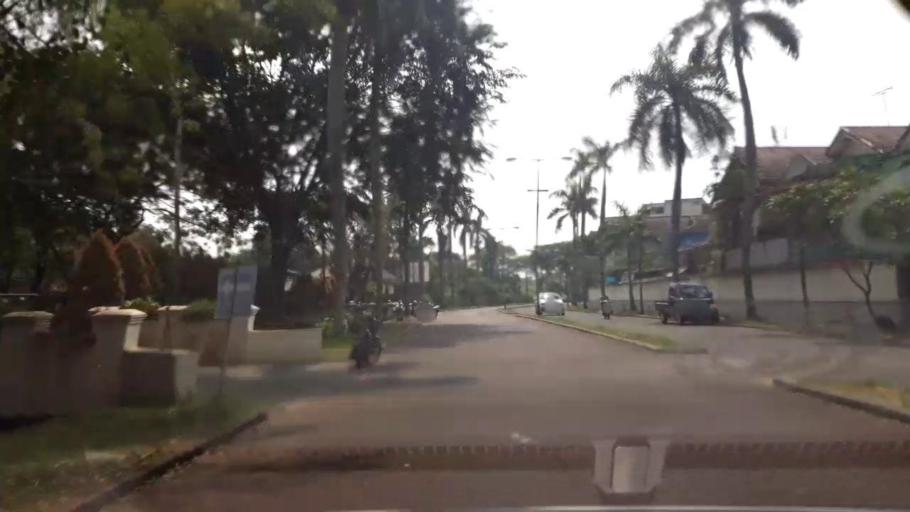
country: ID
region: Banten
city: Curug
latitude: -6.2241
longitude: 106.5873
